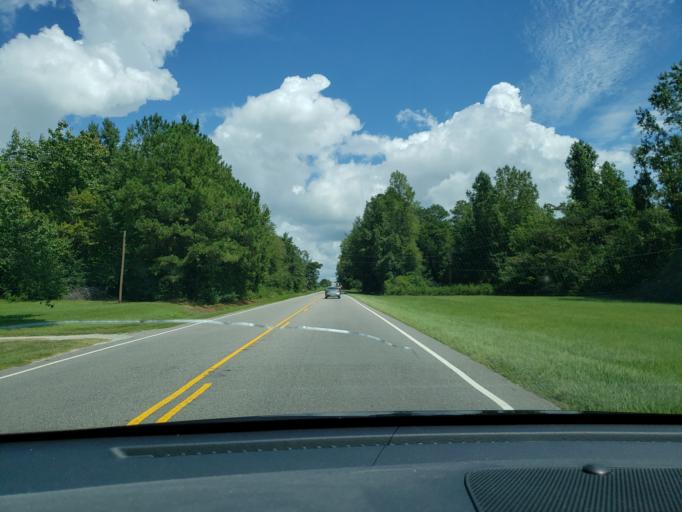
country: US
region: North Carolina
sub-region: Columbus County
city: Brunswick
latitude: 34.2506
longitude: -78.7531
